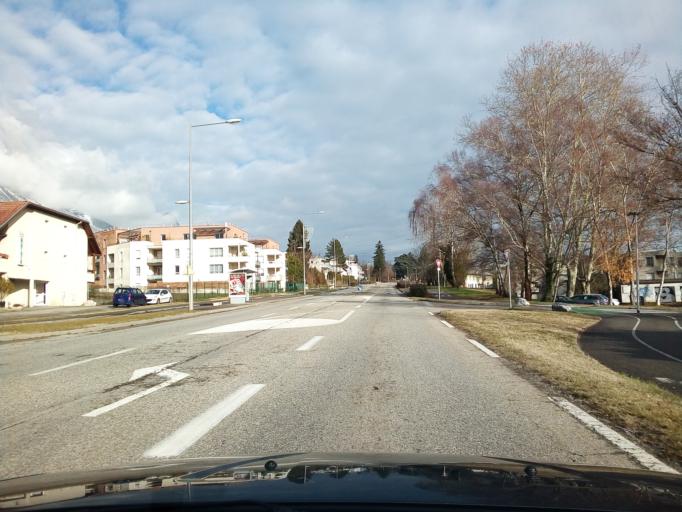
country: FR
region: Rhone-Alpes
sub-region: Departement de l'Isere
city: Corenc
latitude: 45.2112
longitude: 5.7736
